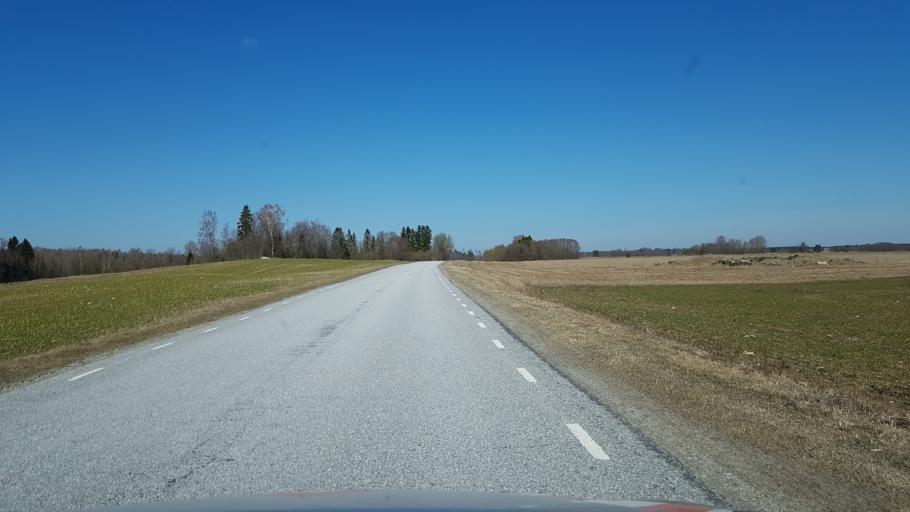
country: EE
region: Jaervamaa
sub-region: Koeru vald
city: Koeru
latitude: 59.0121
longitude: 26.0888
